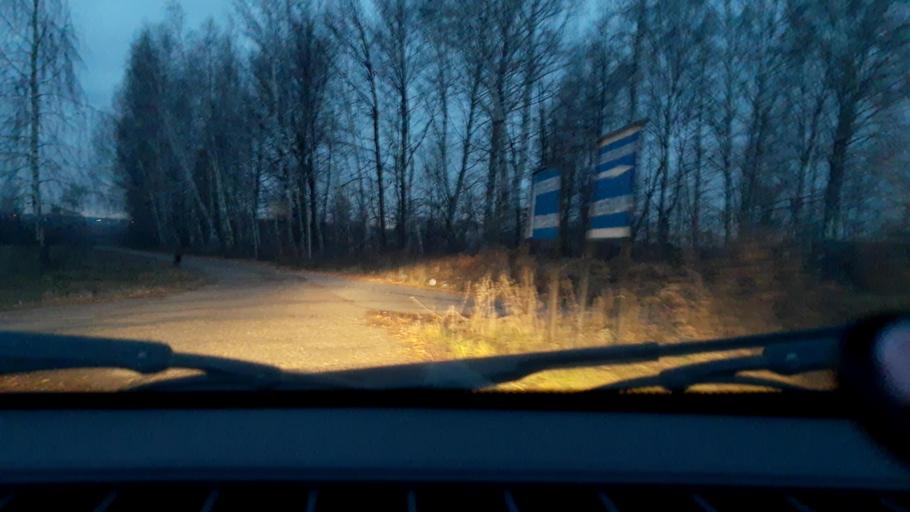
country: RU
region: Bashkortostan
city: Mikhaylovka
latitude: 54.8340
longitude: 55.8560
